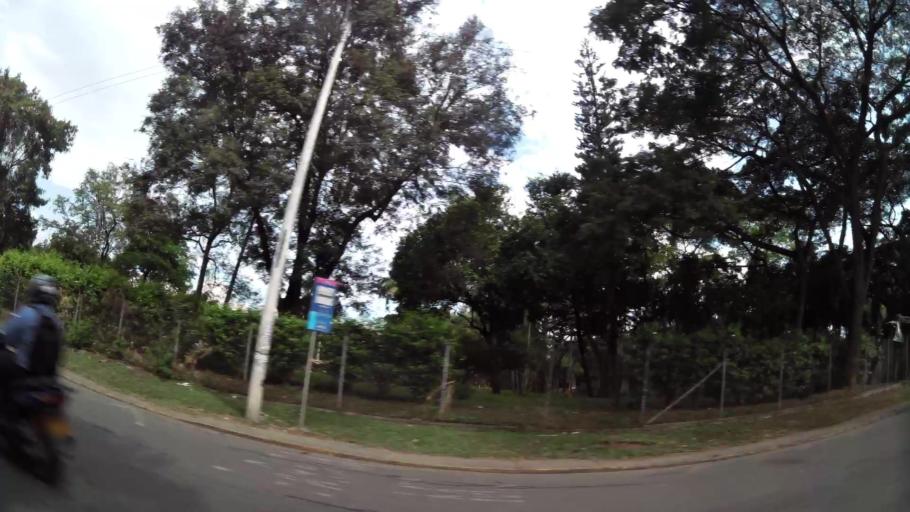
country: CO
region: Valle del Cauca
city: Cali
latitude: 3.4725
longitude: -76.5162
